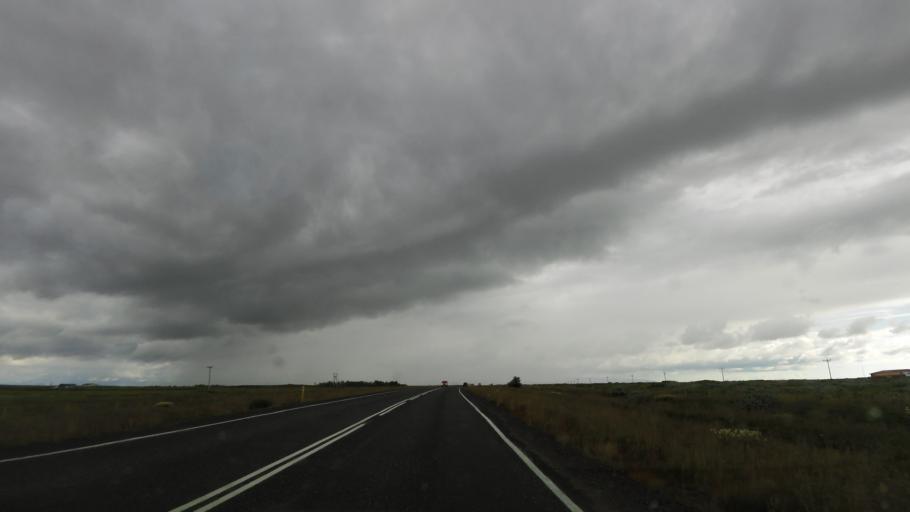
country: IS
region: South
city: Selfoss
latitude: 63.8901
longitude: -20.5387
